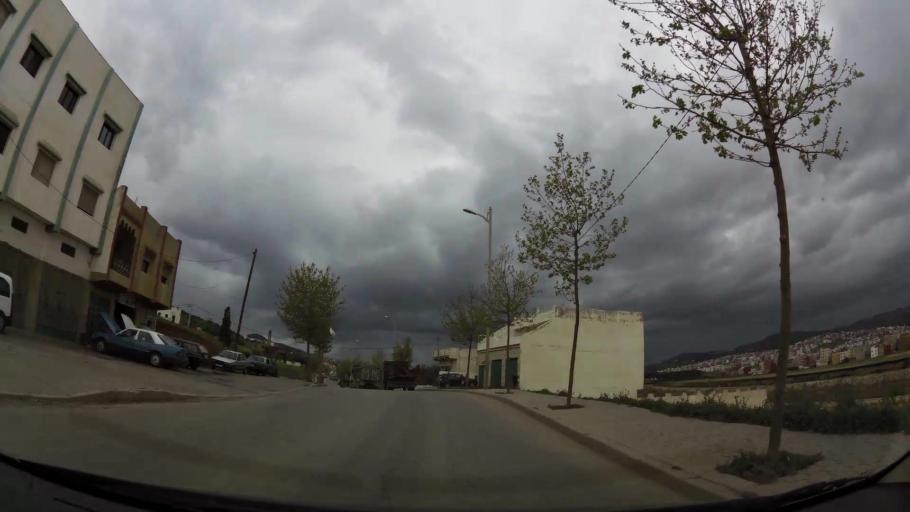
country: MA
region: Tanger-Tetouan
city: Tetouan
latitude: 35.5562
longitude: -5.3921
